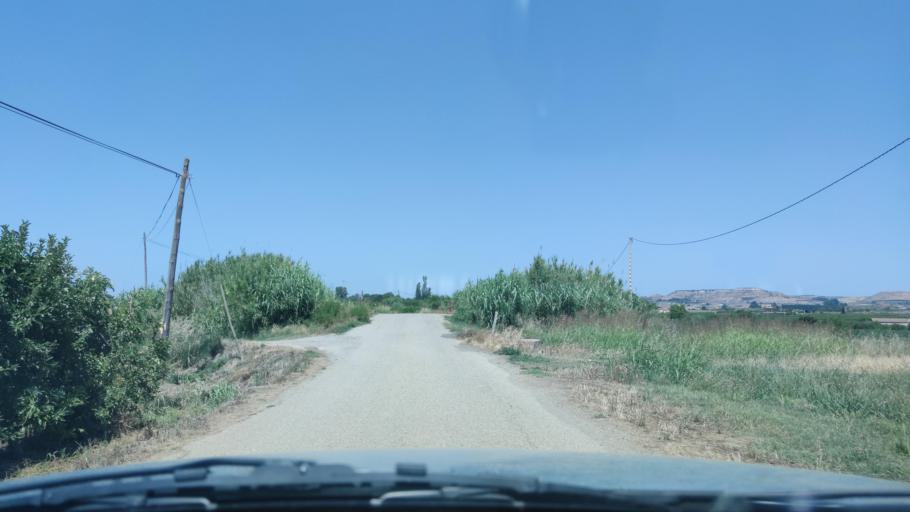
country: ES
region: Catalonia
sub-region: Provincia de Lleida
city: Torrefarrera
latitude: 41.6491
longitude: 0.5957
